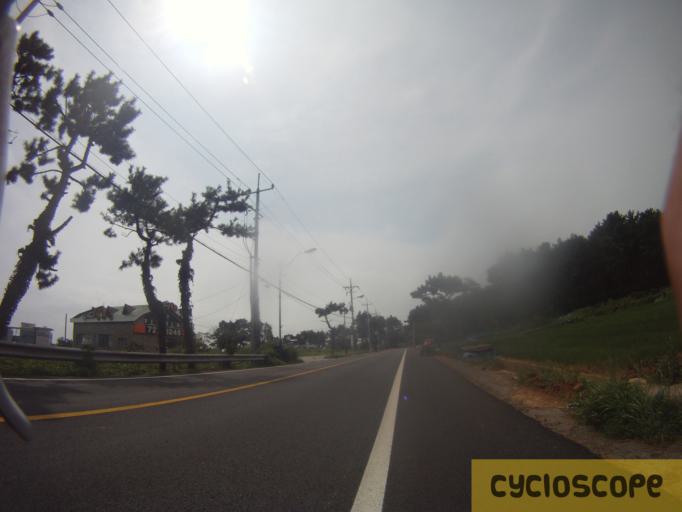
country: KR
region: Busan
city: Kijang
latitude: 35.2814
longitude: 129.2552
